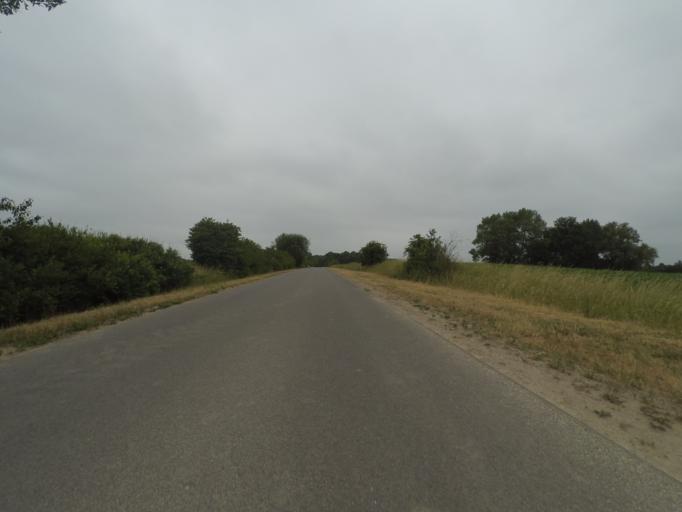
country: DE
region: Mecklenburg-Vorpommern
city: Goldberg
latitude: 53.5469
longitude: 12.1304
